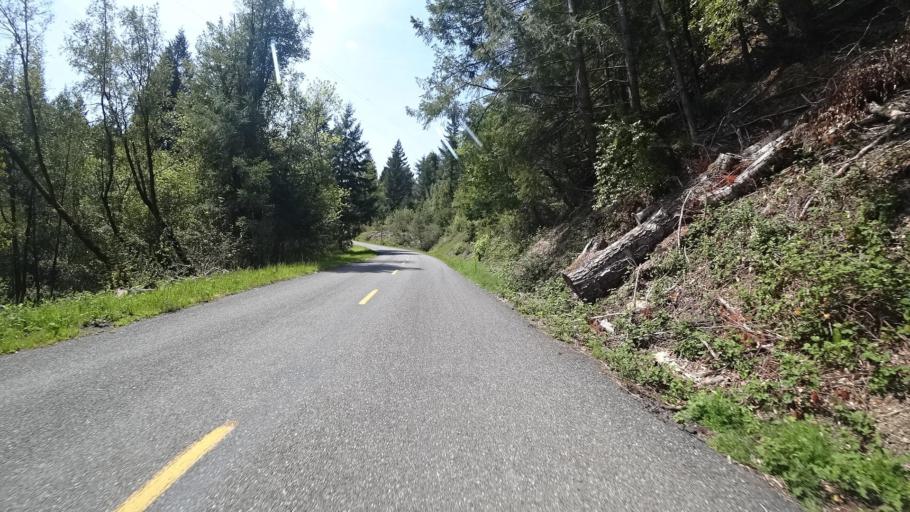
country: US
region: California
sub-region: Humboldt County
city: Redway
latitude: 40.3392
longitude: -123.6953
